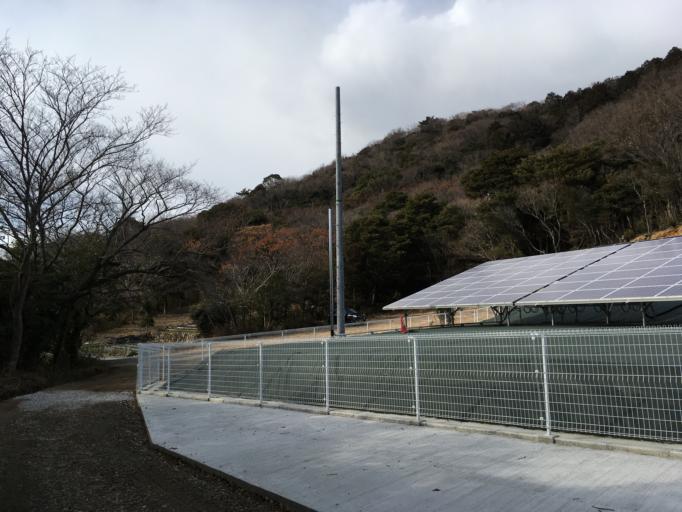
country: JP
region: Aichi
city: Toyohashi
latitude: 34.7284
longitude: 137.4409
